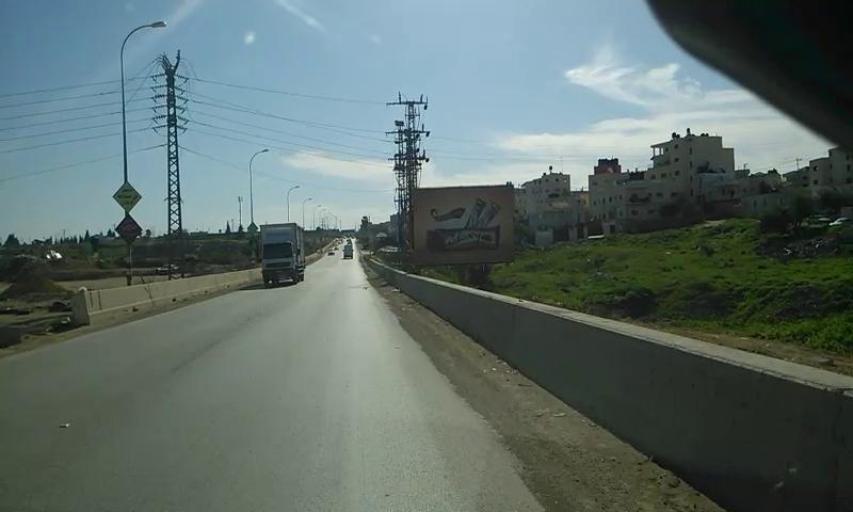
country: PS
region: West Bank
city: Ar Ram wa Dahiyat al Barid
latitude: 31.8577
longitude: 35.2365
